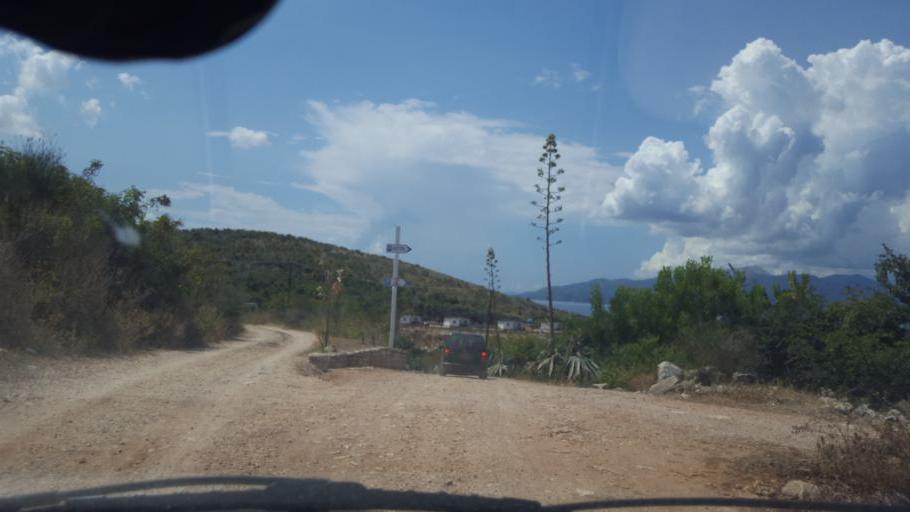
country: AL
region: Vlore
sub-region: Rrethi i Sarandes
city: Sarande
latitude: 39.8396
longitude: 20.0127
